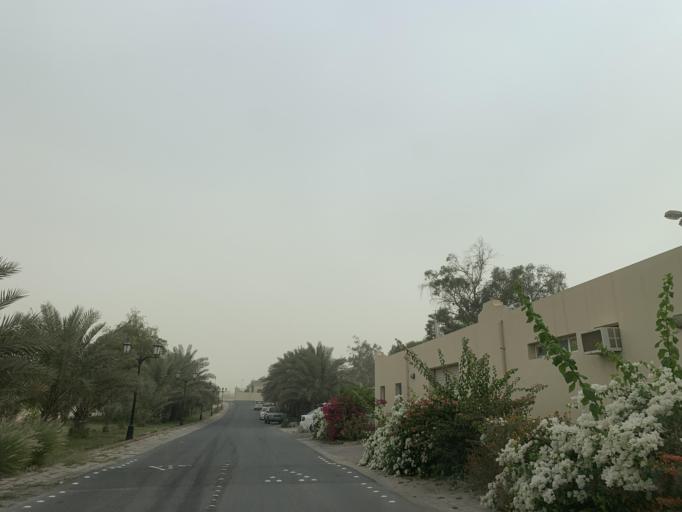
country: BH
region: Northern
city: Ar Rifa'
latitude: 26.1378
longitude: 50.5353
